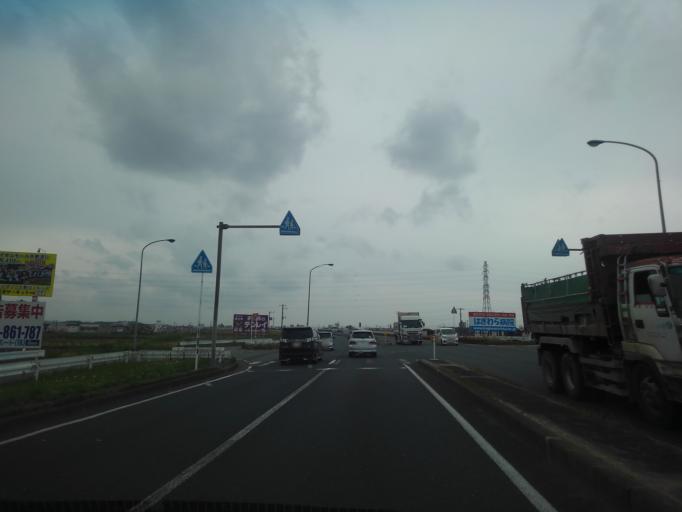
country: JP
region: Chiba
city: Kisarazu
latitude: 35.4046
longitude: 139.9431
